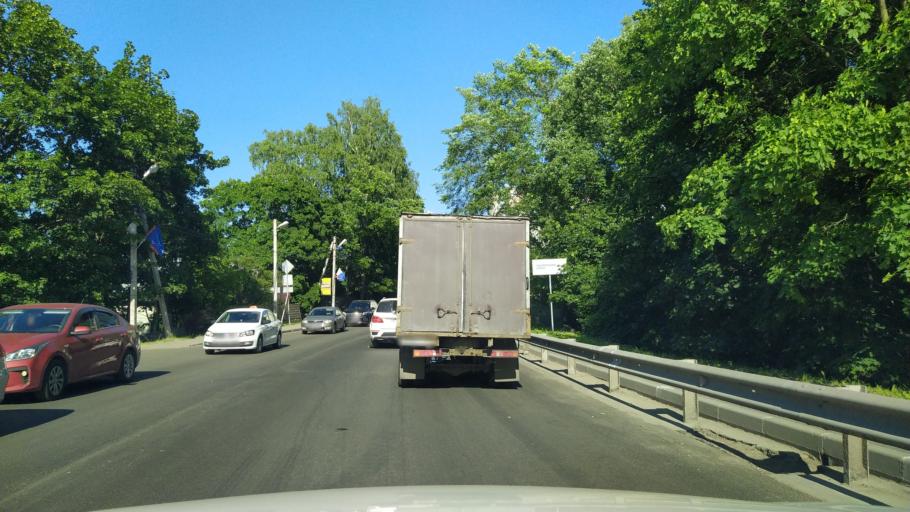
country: RU
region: Leningrad
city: Murino
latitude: 60.0473
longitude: 30.4579
